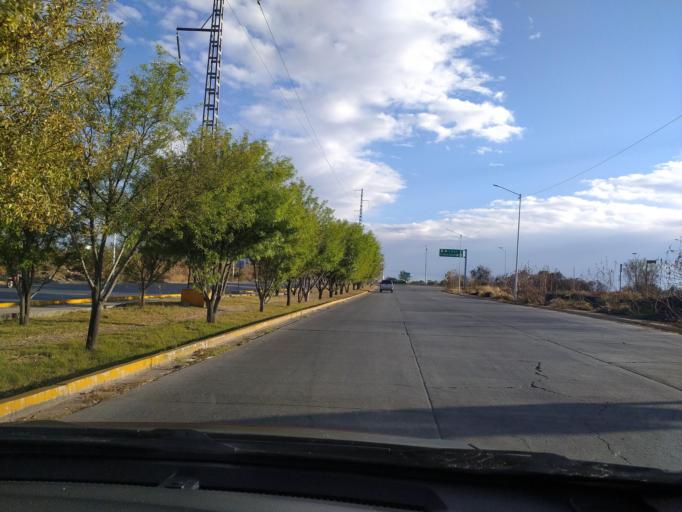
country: MX
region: Guanajuato
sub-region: Purisima del Rincon
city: Monte Grande
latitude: 21.0039
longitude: -101.8703
